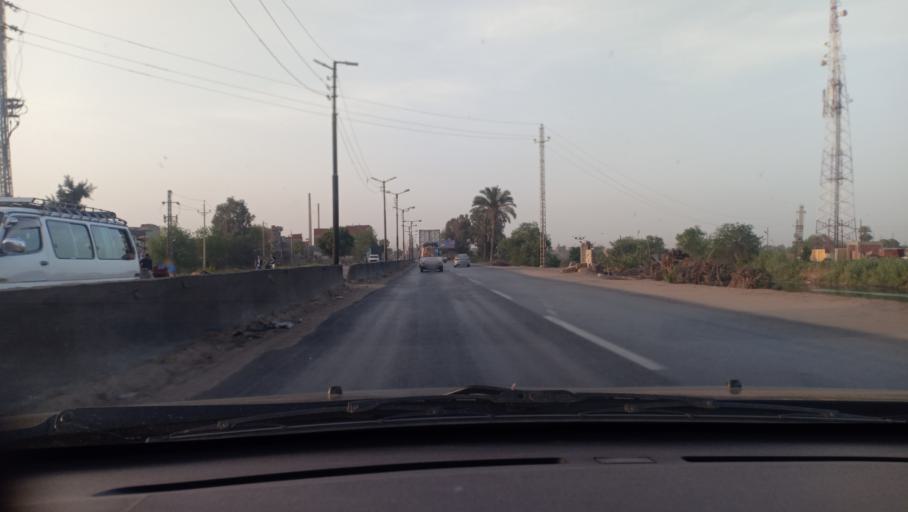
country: EG
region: Muhafazat al Gharbiyah
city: Zifta
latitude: 30.6237
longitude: 31.2788
